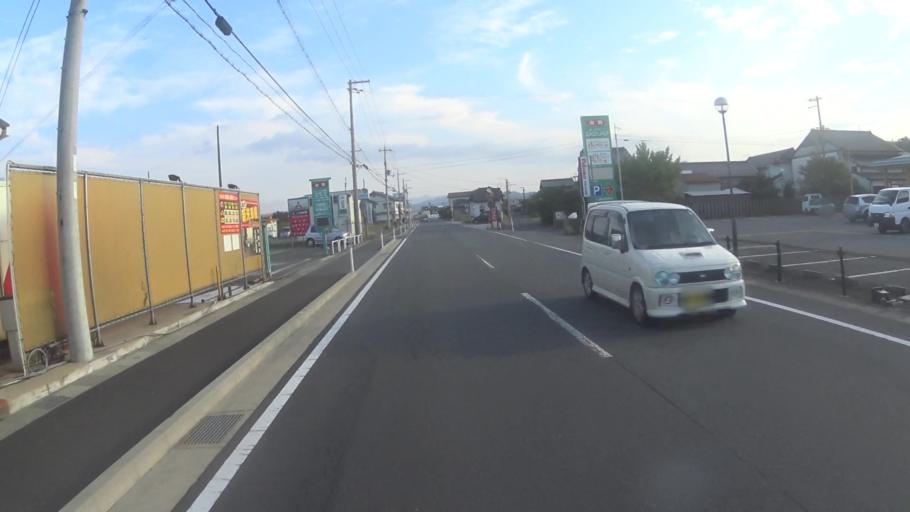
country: JP
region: Kyoto
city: Miyazu
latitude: 35.6225
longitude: 135.0739
